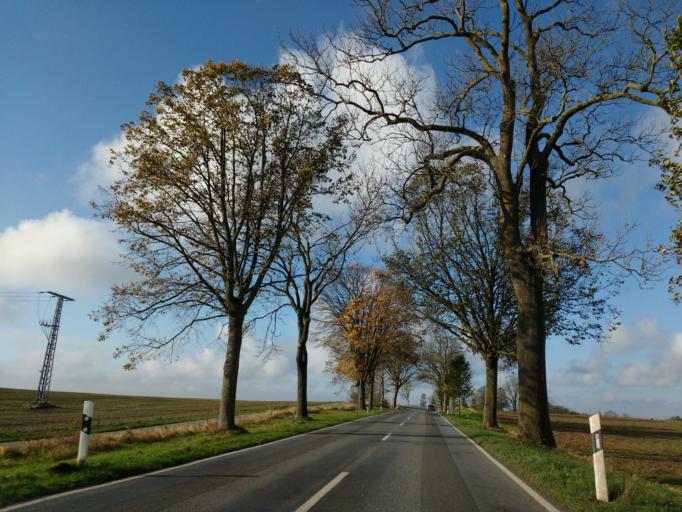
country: DE
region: Mecklenburg-Vorpommern
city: Klutz
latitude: 53.9615
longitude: 11.1875
